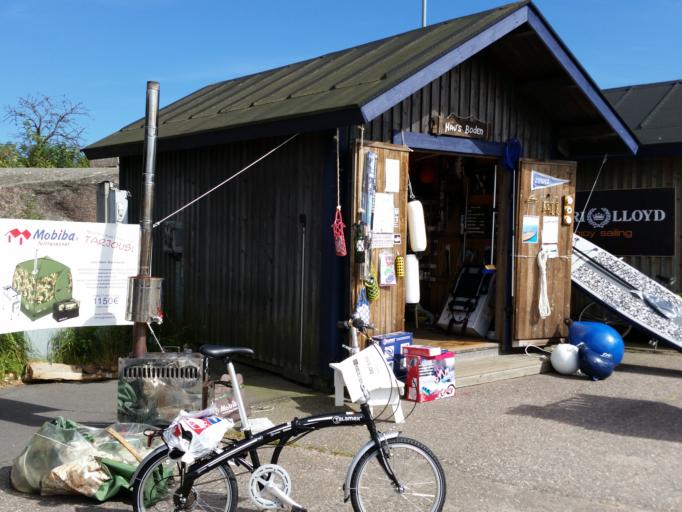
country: FI
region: Uusimaa
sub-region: Raaseporin
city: Hanko
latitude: 59.8202
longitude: 22.9679
